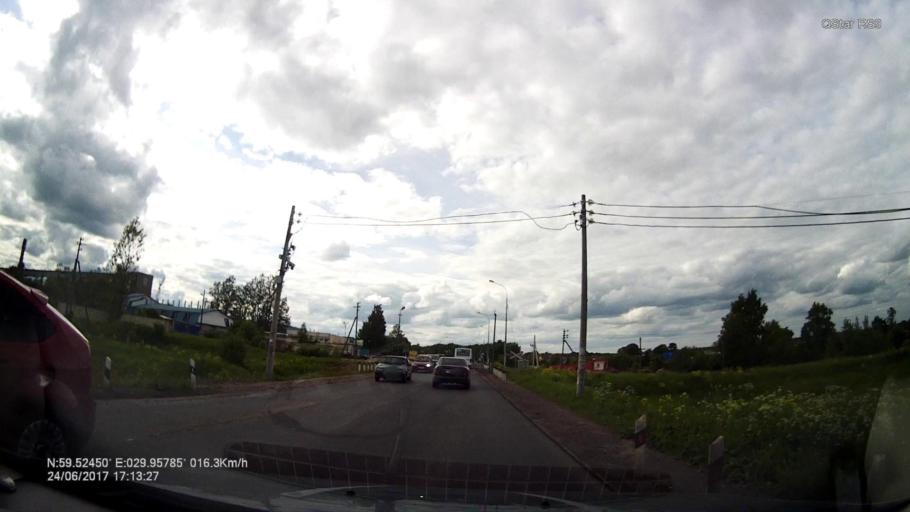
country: RU
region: Leningrad
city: Voyskovitsy
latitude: 59.5245
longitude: 29.9577
